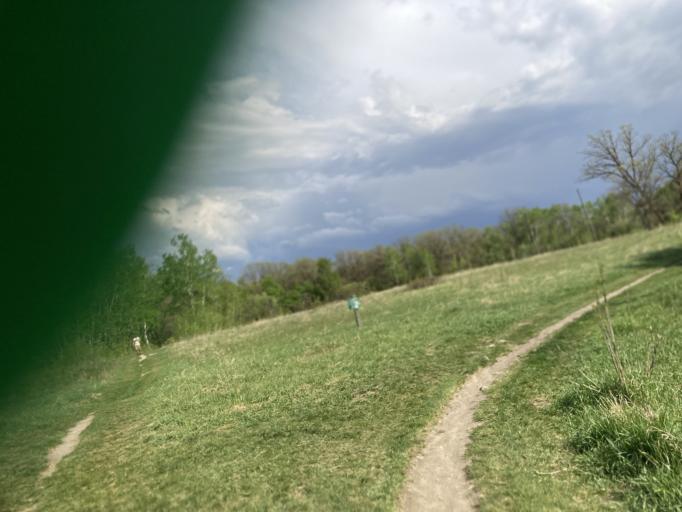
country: CA
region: Manitoba
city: Brandon
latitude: 49.7240
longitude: -99.9092
